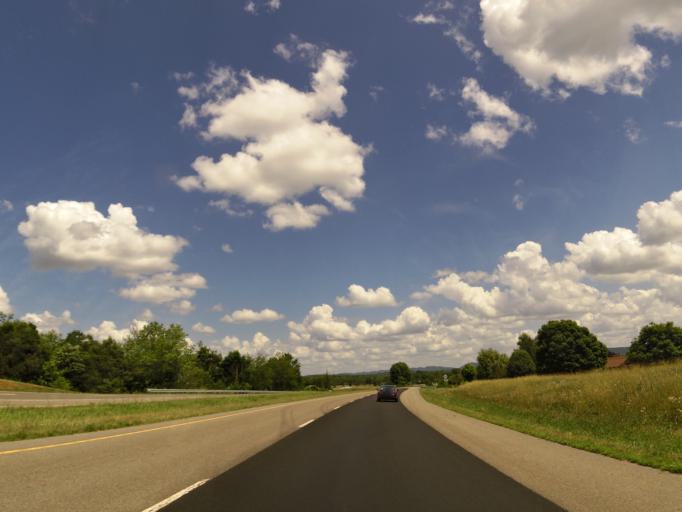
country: US
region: Virginia
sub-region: Lee County
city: Jonesville
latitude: 36.6703
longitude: -83.1966
